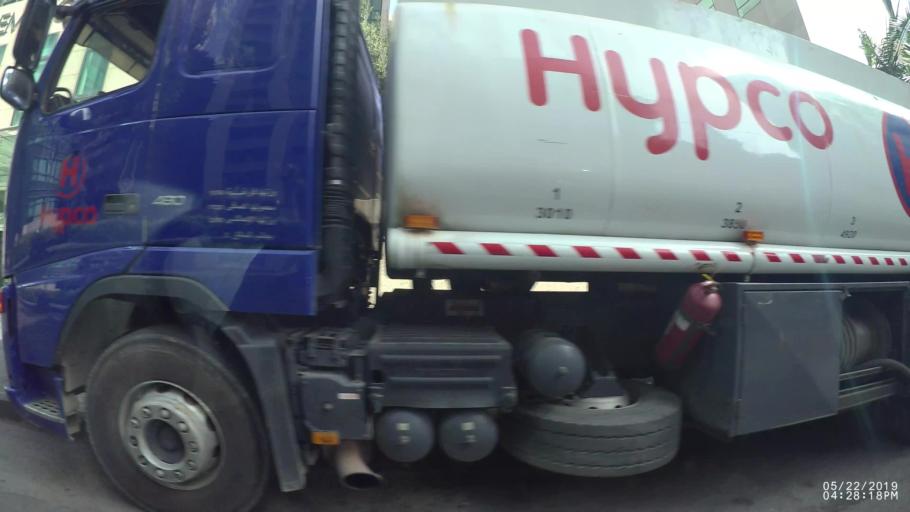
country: LB
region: Beyrouth
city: Ra's Bayrut
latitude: 33.8979
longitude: 35.4900
